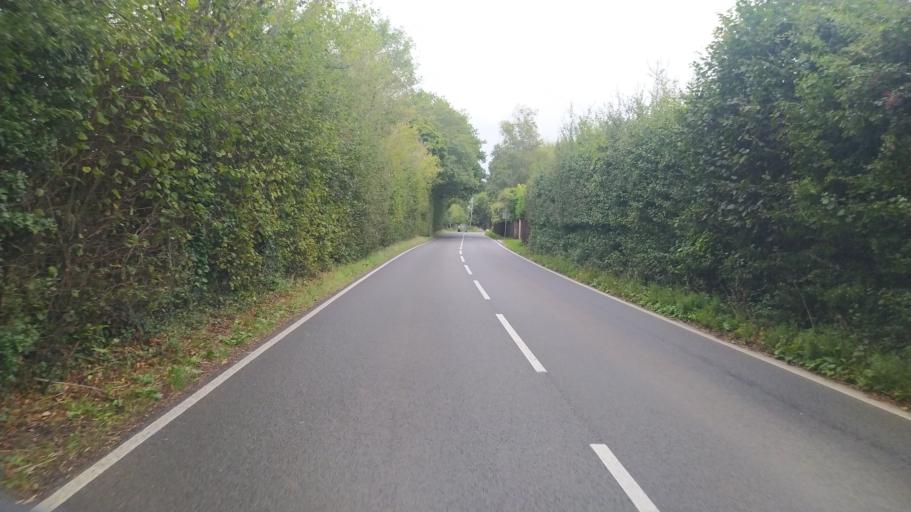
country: GB
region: England
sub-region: Dorset
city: Sherborne
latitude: 50.8635
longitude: -2.4695
